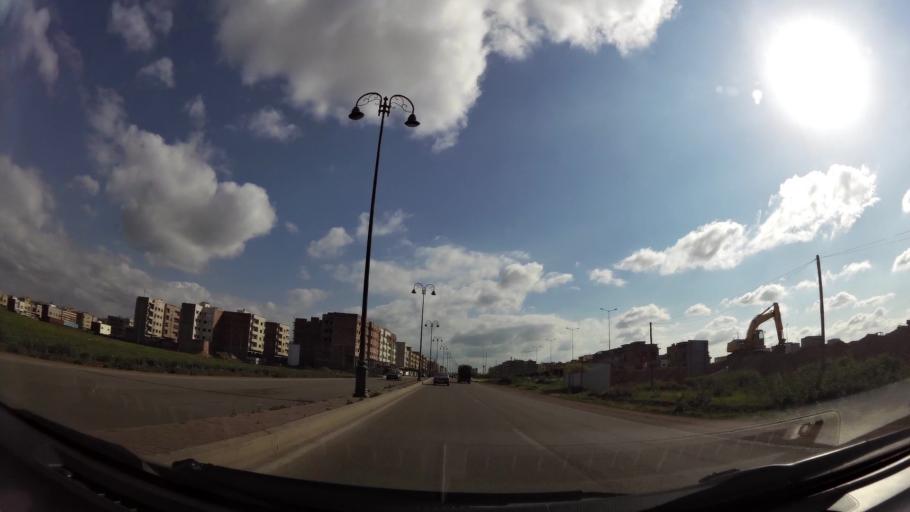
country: MA
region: Chaouia-Ouardigha
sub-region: Settat Province
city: Berrechid
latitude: 33.2800
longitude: -7.5806
